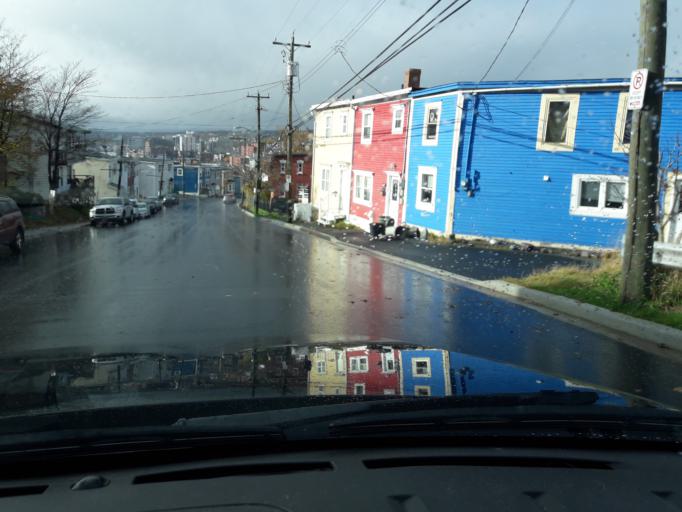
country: CA
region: Newfoundland and Labrador
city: St. John's
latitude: 47.5727
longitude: -52.6949
